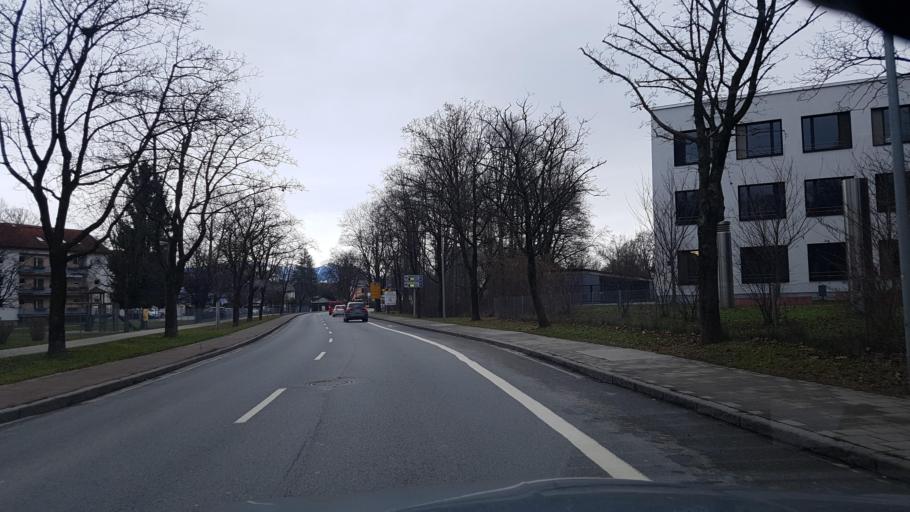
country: DE
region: Bavaria
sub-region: Upper Bavaria
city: Rosenheim
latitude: 47.8633
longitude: 12.1101
